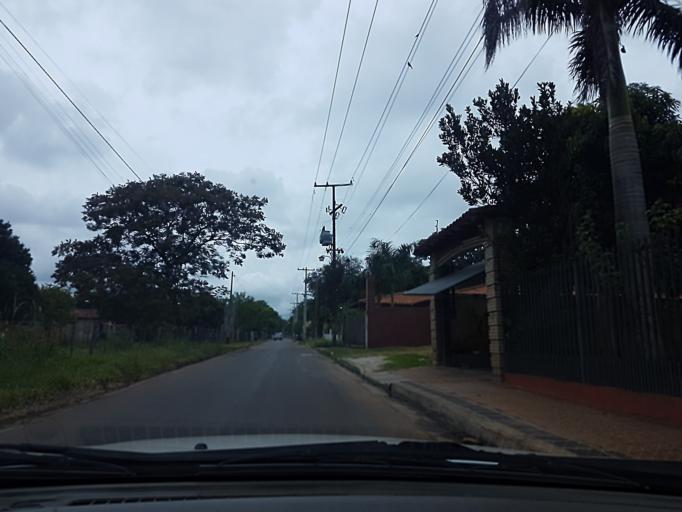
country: PY
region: Central
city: Limpio
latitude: -25.1839
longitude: -57.4696
